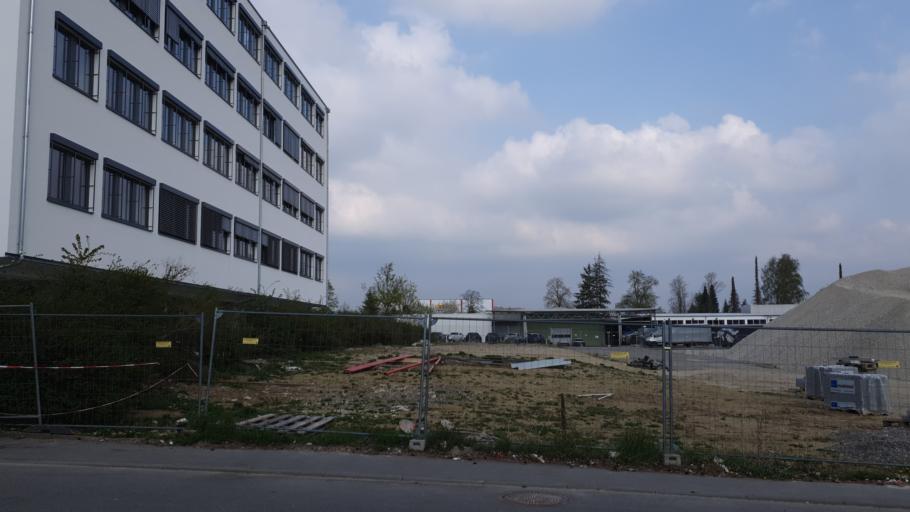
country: DE
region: Baden-Wuerttemberg
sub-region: Regierungsbezirk Stuttgart
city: Renningen
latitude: 48.7758
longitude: 8.9260
